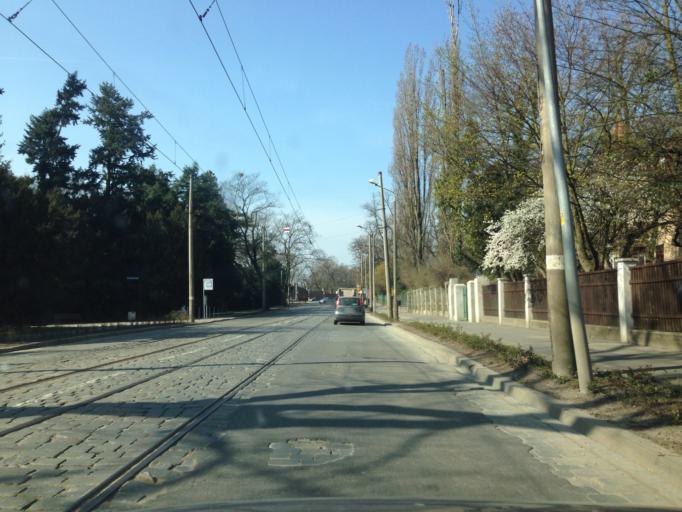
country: PL
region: Lower Silesian Voivodeship
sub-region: Powiat wroclawski
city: Wroclaw
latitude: 51.1088
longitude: 17.0733
